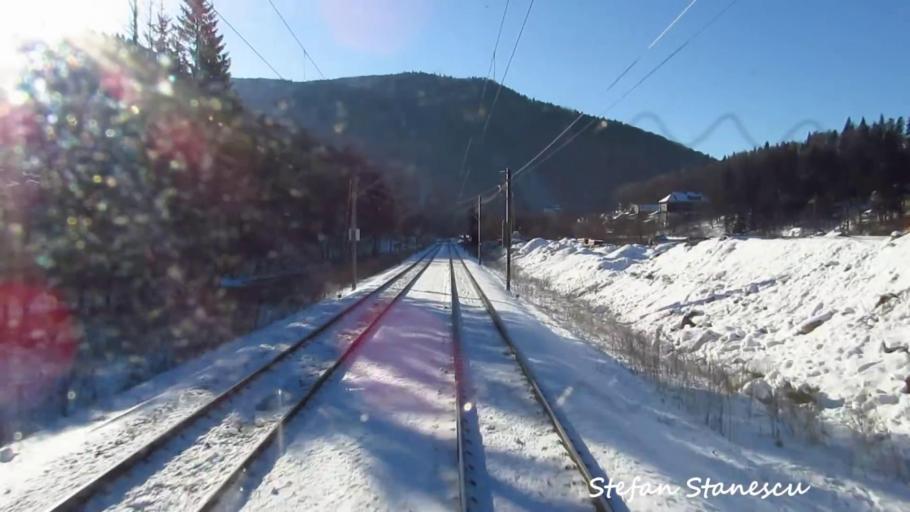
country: RO
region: Prahova
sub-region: Oras Sinaia
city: Sinaia
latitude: 45.3683
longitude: 25.5457
